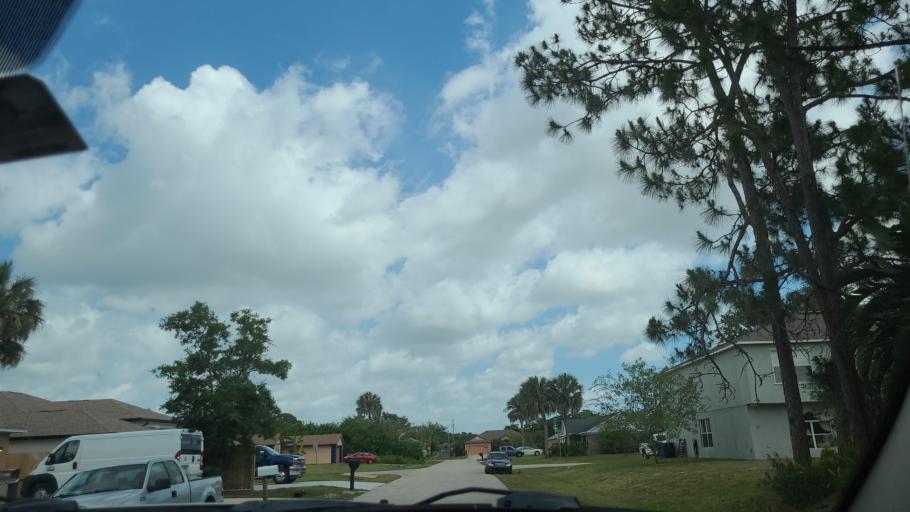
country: US
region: Florida
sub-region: Brevard County
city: West Melbourne
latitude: 28.0042
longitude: -80.6573
